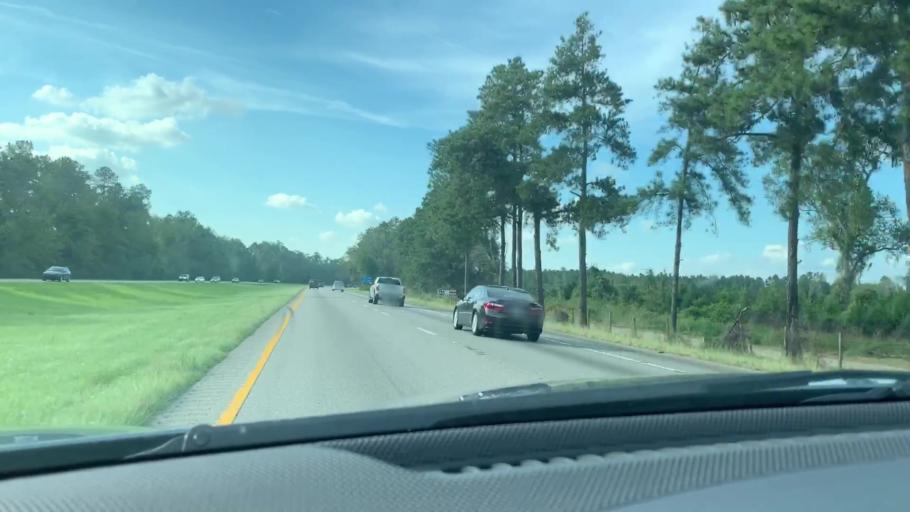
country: US
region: South Carolina
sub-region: Orangeburg County
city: Brookdale
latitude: 33.4721
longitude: -80.7484
